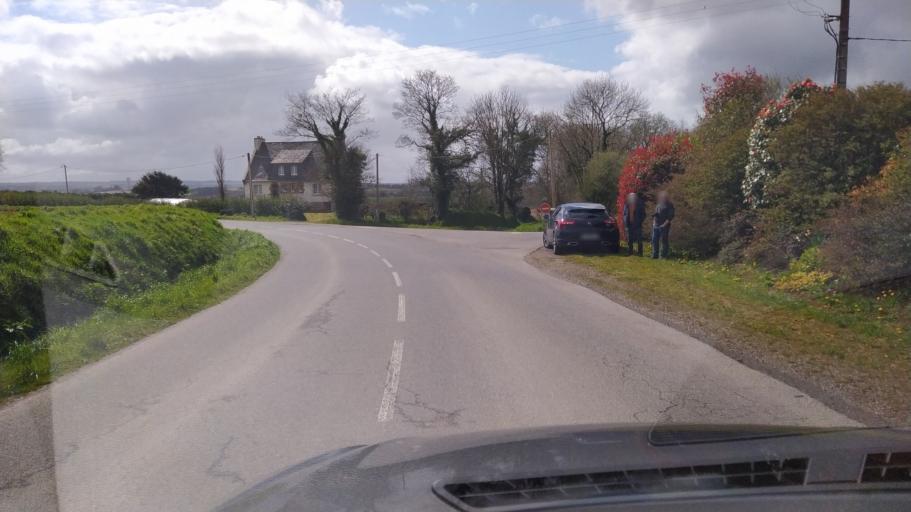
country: FR
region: Brittany
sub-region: Departement du Finistere
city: Bodilis
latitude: 48.5255
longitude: -4.1238
